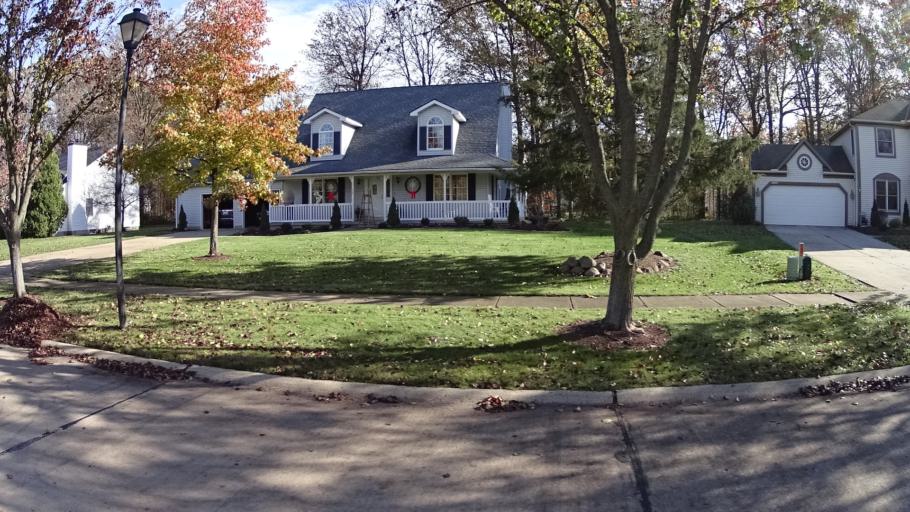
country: US
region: Ohio
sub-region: Lorain County
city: Avon Lake
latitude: 41.4954
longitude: -82.0443
